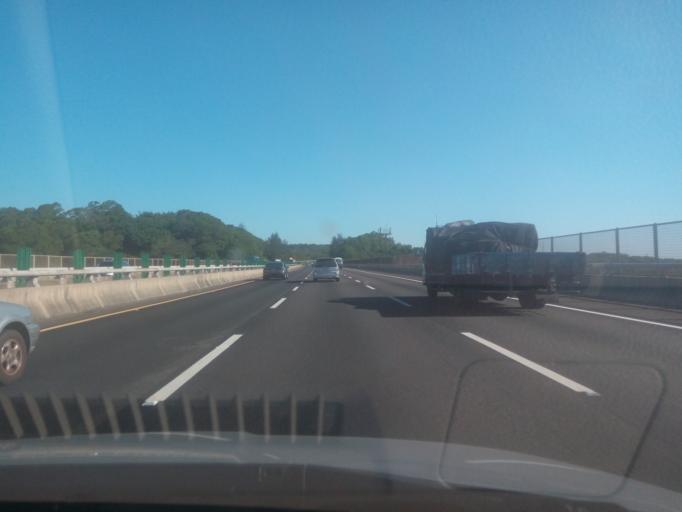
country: TW
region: Taiwan
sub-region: Hsinchu
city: Hsinchu
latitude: 24.7444
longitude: 120.9244
